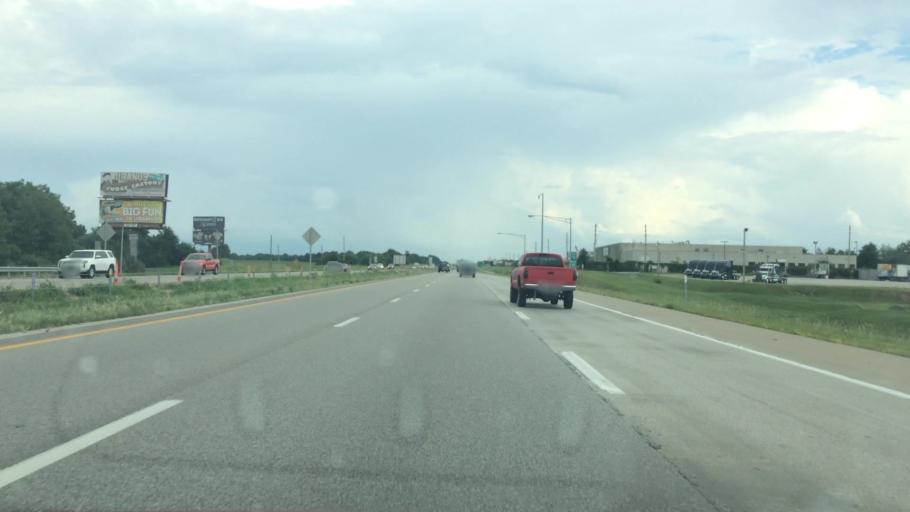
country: US
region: Missouri
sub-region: Greene County
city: Springfield
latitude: 37.2501
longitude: -93.2164
